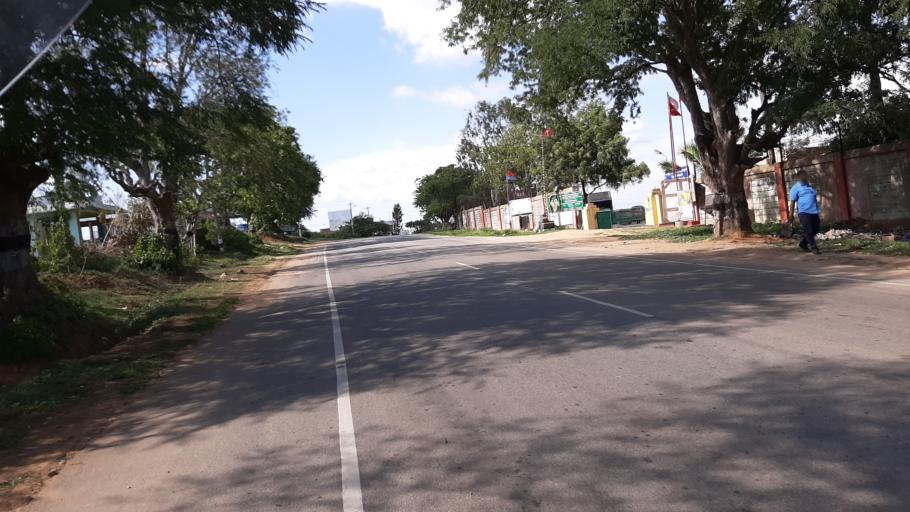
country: IN
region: Tamil Nadu
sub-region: Krishnagiri
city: Denkanikota
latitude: 12.5373
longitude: 77.7889
